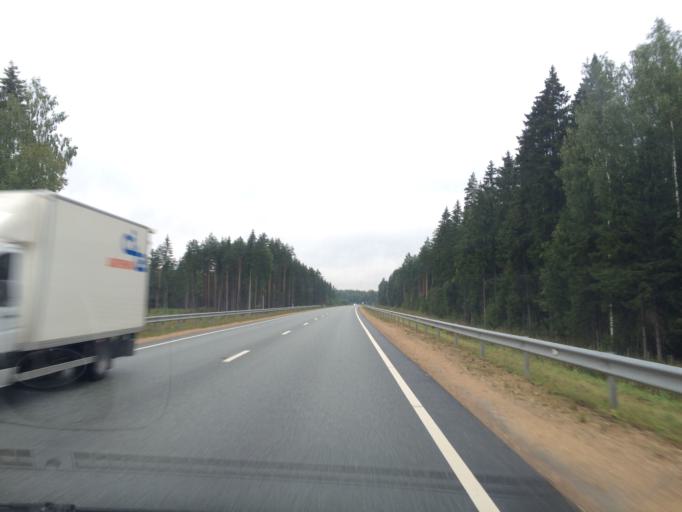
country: LV
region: Ogre
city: Ogre
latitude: 56.8524
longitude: 24.6541
